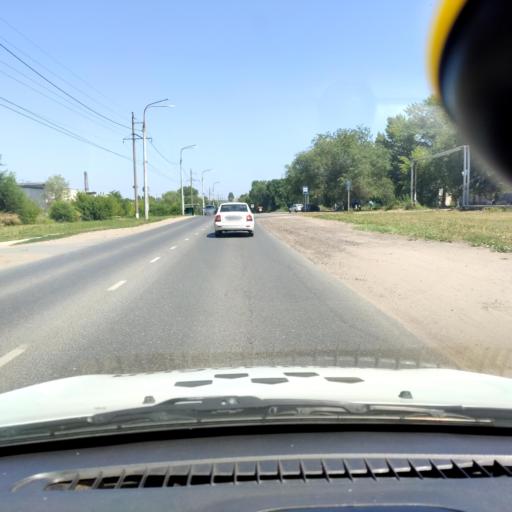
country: RU
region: Samara
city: Zhigulevsk
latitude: 53.4041
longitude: 49.5209
